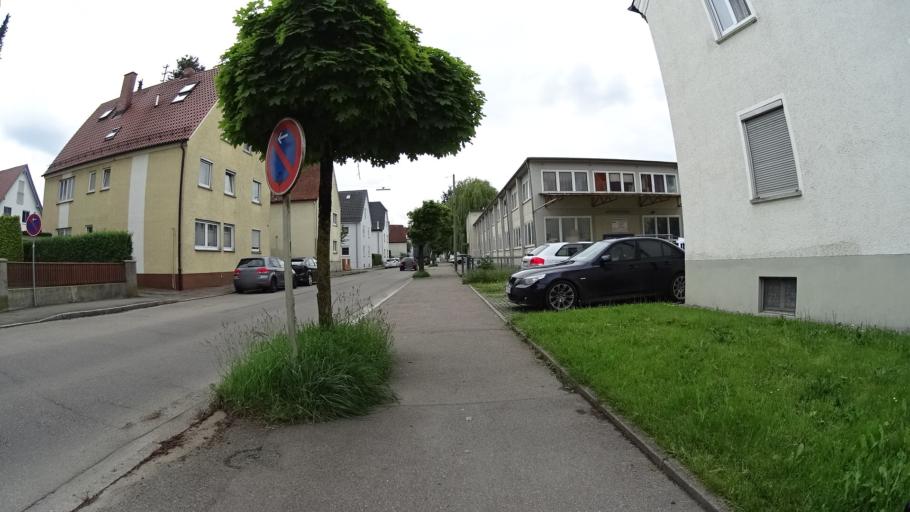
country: DE
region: Bavaria
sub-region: Swabia
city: Weissenhorn
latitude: 48.3105
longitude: 10.1576
